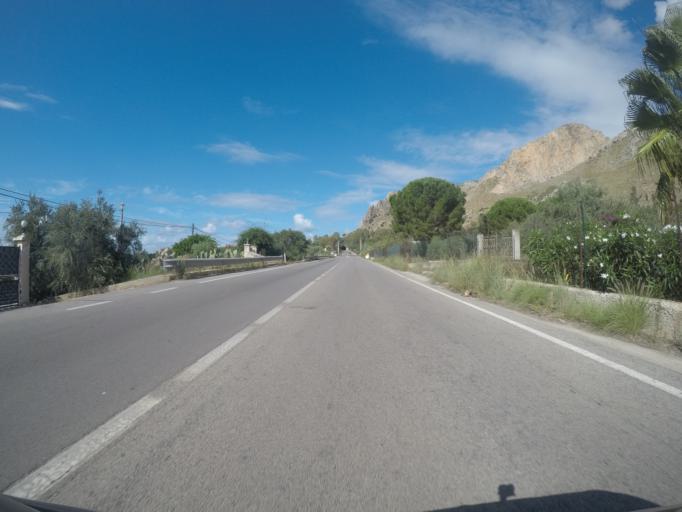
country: IT
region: Sicily
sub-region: Palermo
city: Agliandroni-Paternella
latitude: 38.1199
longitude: 13.0760
